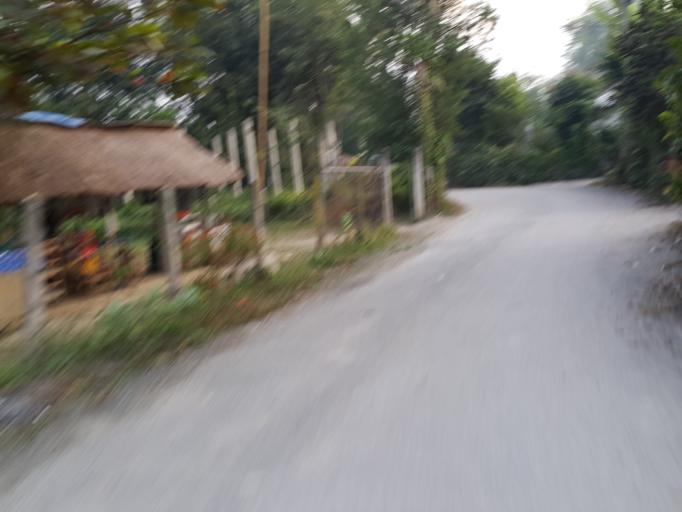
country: TH
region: Chiang Mai
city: San Sai
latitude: 18.8334
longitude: 99.1086
